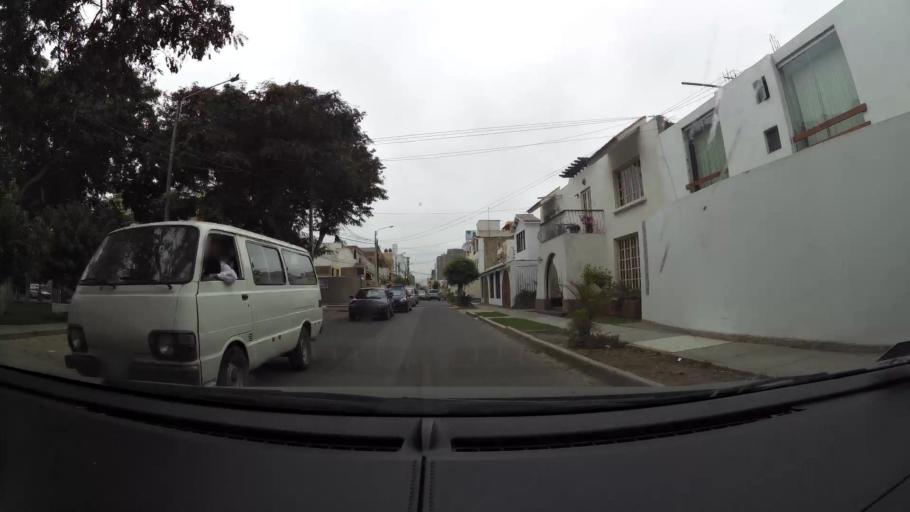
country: PE
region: La Libertad
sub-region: Provincia de Trujillo
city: Buenos Aires
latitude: -8.1321
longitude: -79.0386
